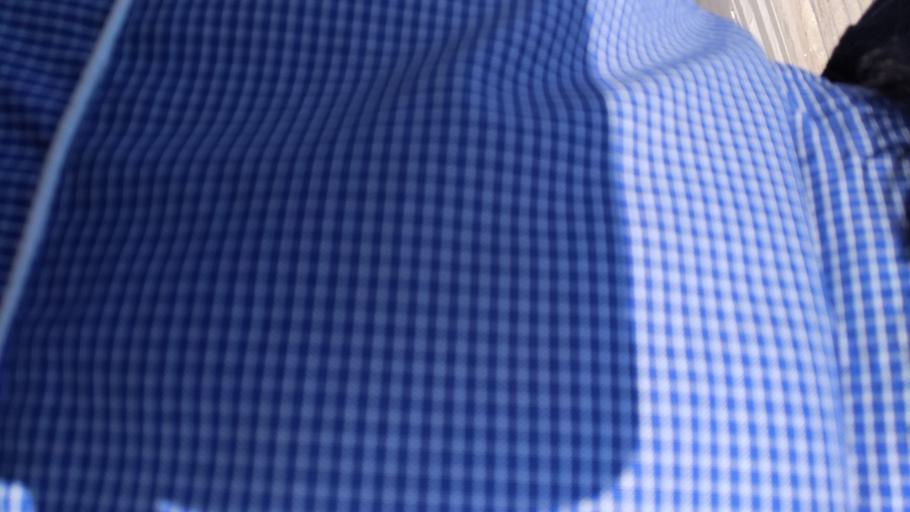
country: IN
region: Telangana
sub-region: Rangareddi
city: Lal Bahadur Nagar
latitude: 17.3331
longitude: 78.5695
